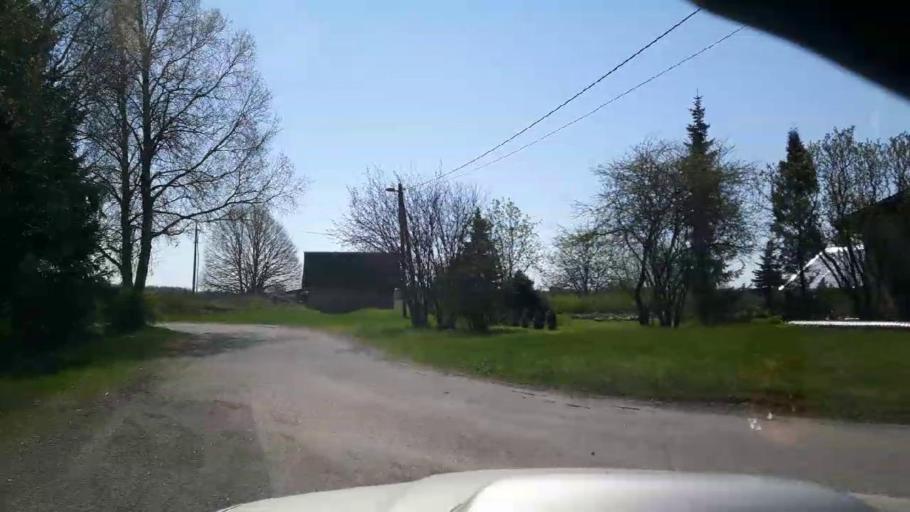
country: EE
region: Paernumaa
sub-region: Tootsi vald
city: Tootsi
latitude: 58.4766
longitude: 24.7948
